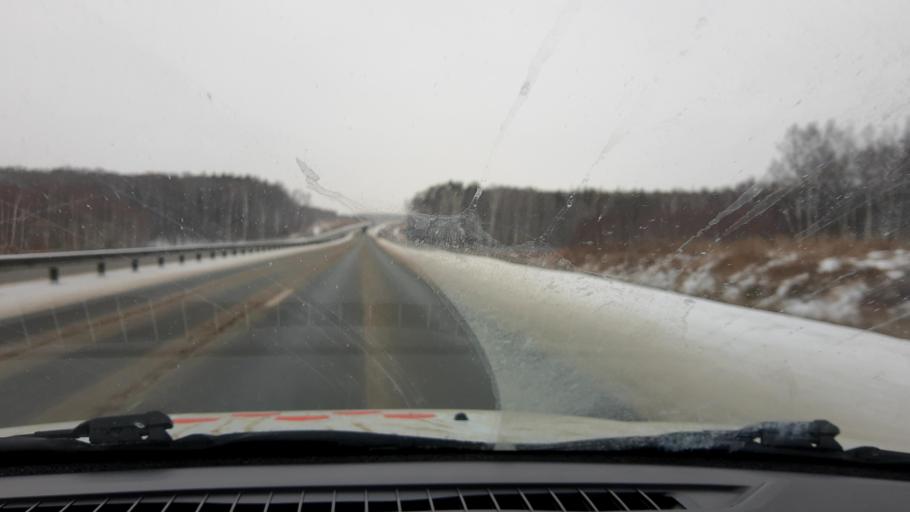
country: RU
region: Nizjnij Novgorod
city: Afonino
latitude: 56.1064
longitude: 43.9933
